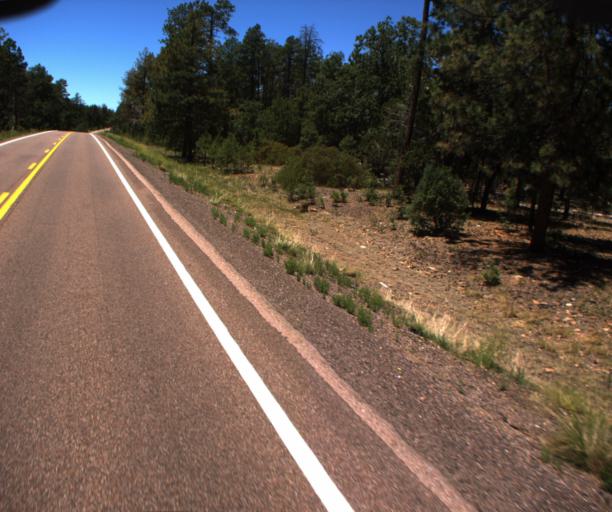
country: US
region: Arizona
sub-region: Gila County
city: Pine
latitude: 34.4406
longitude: -111.4764
